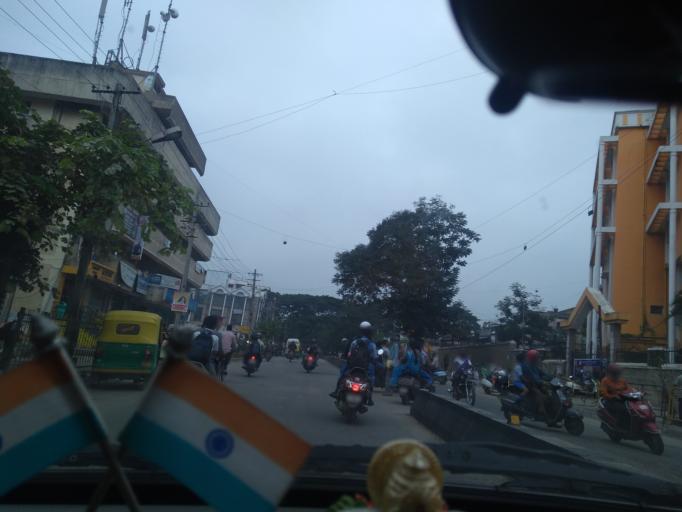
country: IN
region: Karnataka
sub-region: Bangalore Urban
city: Bangalore
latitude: 12.9812
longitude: 77.5593
